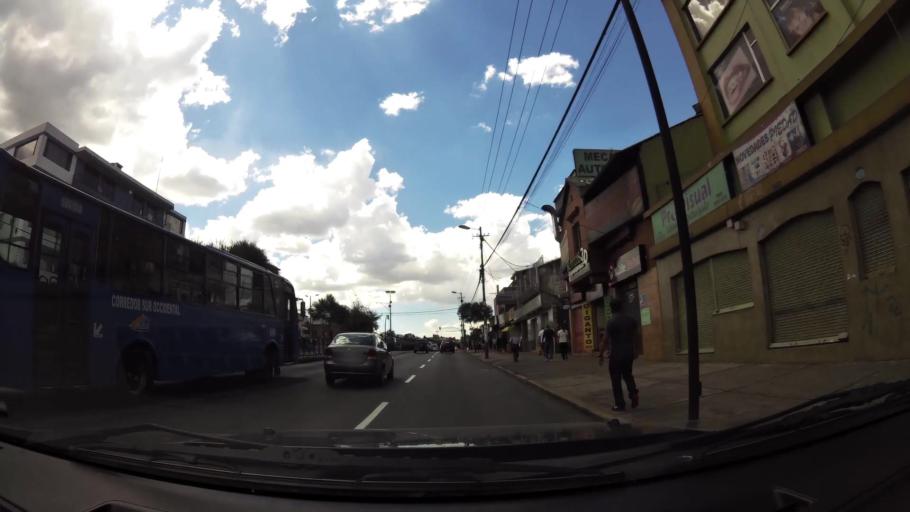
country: EC
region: Pichincha
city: Quito
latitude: -0.1986
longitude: -78.5004
